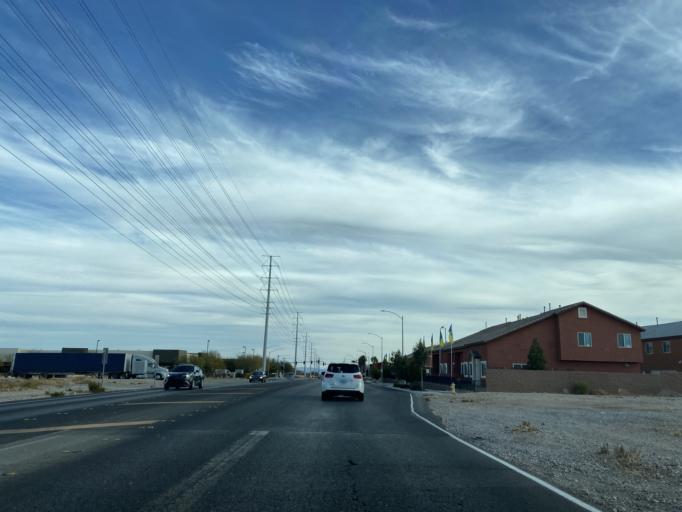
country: US
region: Nevada
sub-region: Clark County
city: Enterprise
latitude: 36.0556
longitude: -115.2549
